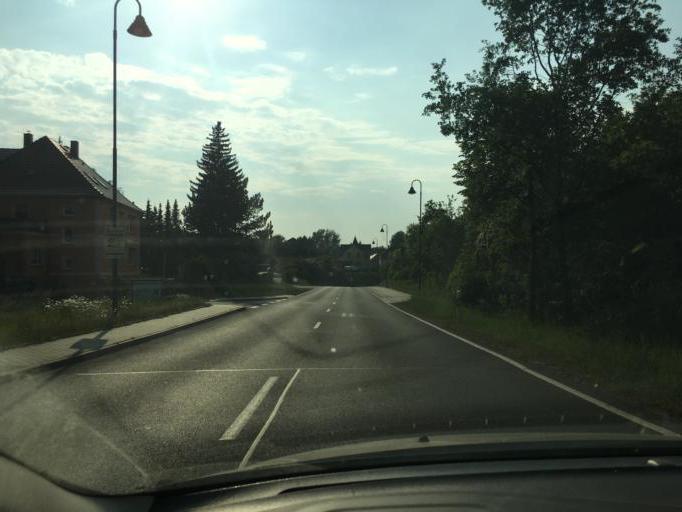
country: DE
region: Saxony
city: Grossbothen
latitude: 51.1838
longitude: 12.7567
